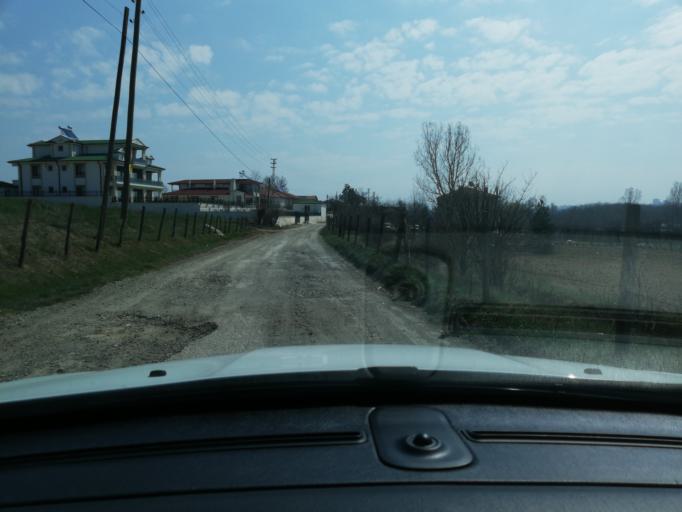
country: TR
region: Kastamonu
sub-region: Cide
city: Kastamonu
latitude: 41.4604
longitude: 33.7549
